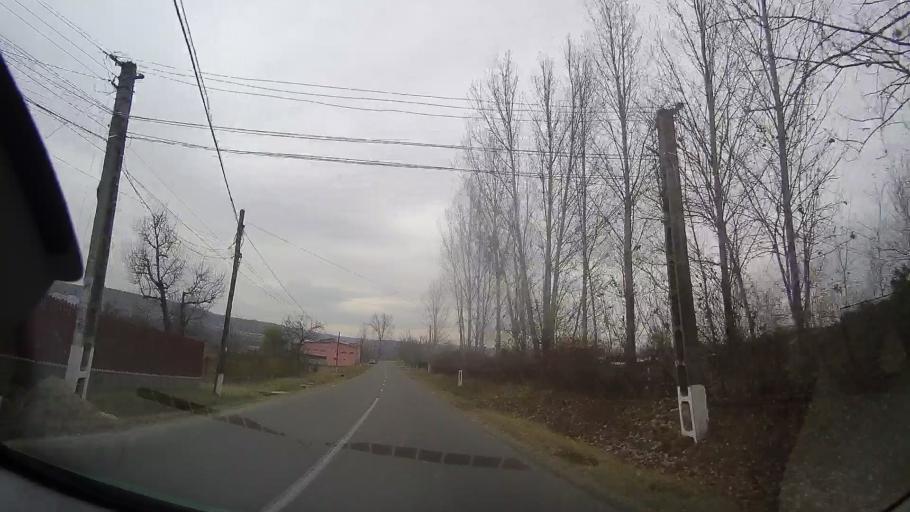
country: RO
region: Prahova
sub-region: Comuna Iordachianu
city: Iordacheanu
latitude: 45.0354
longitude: 26.2395
